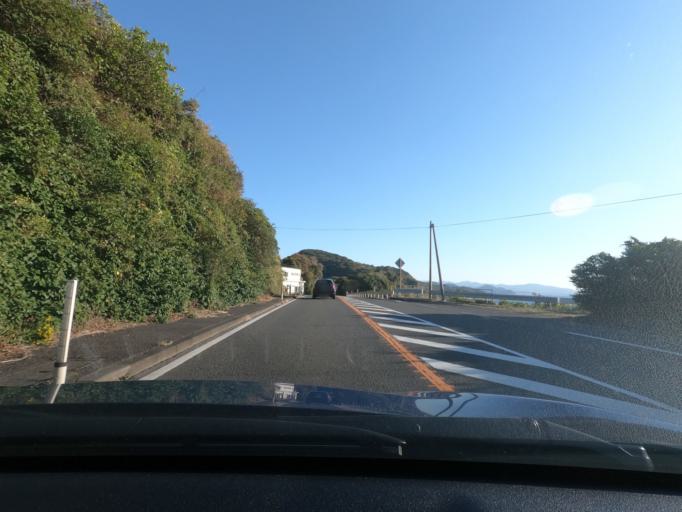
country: JP
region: Kagoshima
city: Akune
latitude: 31.9342
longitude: 130.2194
